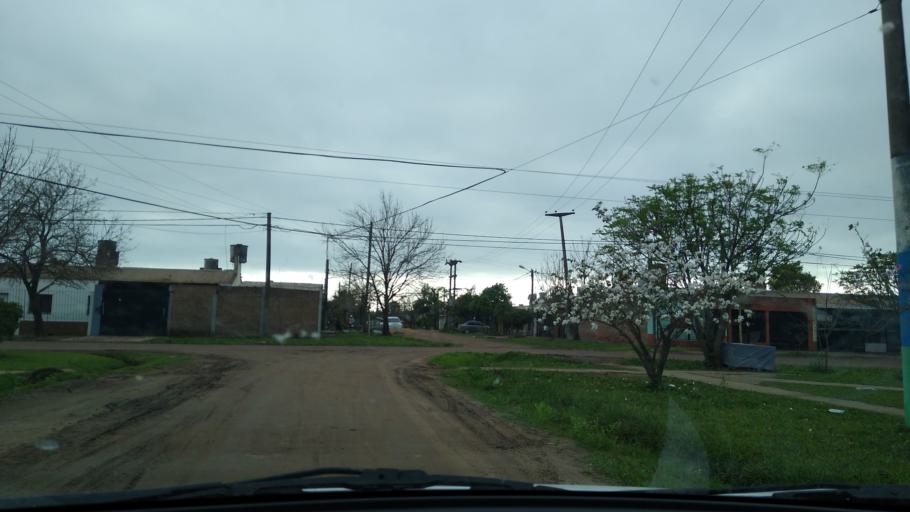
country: AR
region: Chaco
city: Resistencia
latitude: -27.4902
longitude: -58.9802
